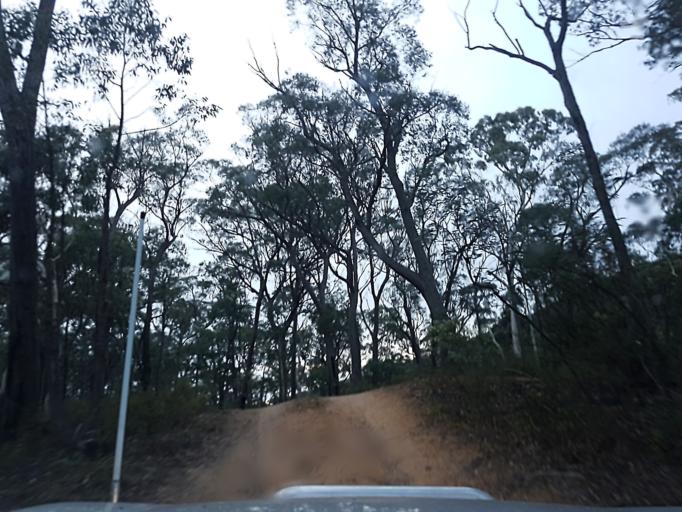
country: AU
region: New South Wales
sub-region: Snowy River
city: Jindabyne
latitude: -36.8638
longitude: 148.2371
